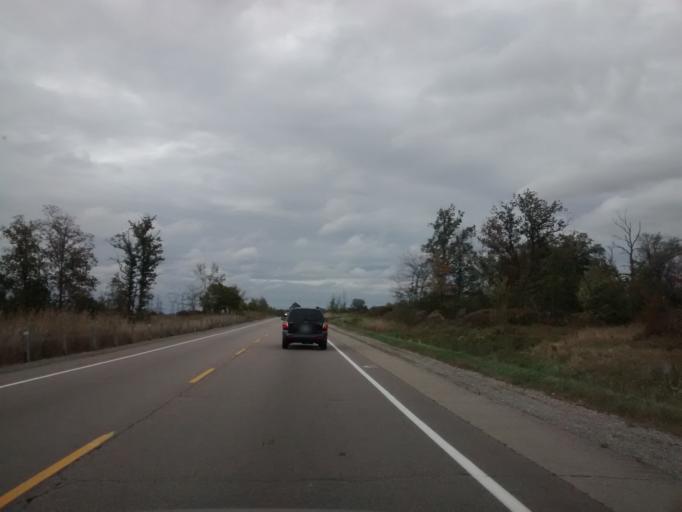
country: CA
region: Ontario
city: Ancaster
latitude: 43.0667
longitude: -79.9784
